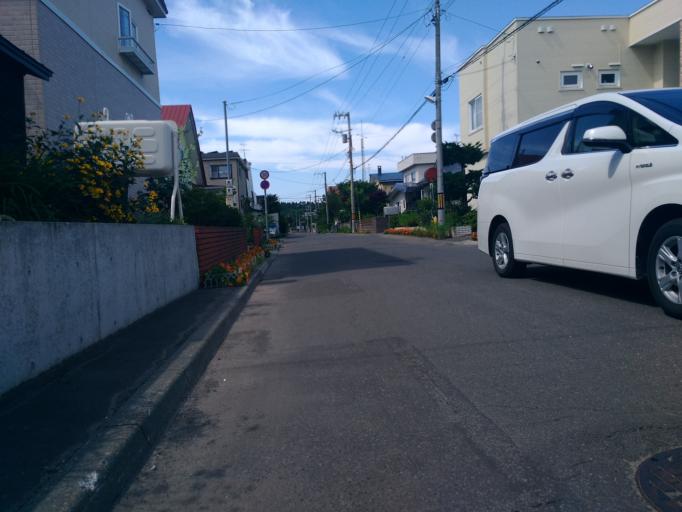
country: JP
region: Hokkaido
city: Ebetsu
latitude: 43.0786
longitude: 141.5009
